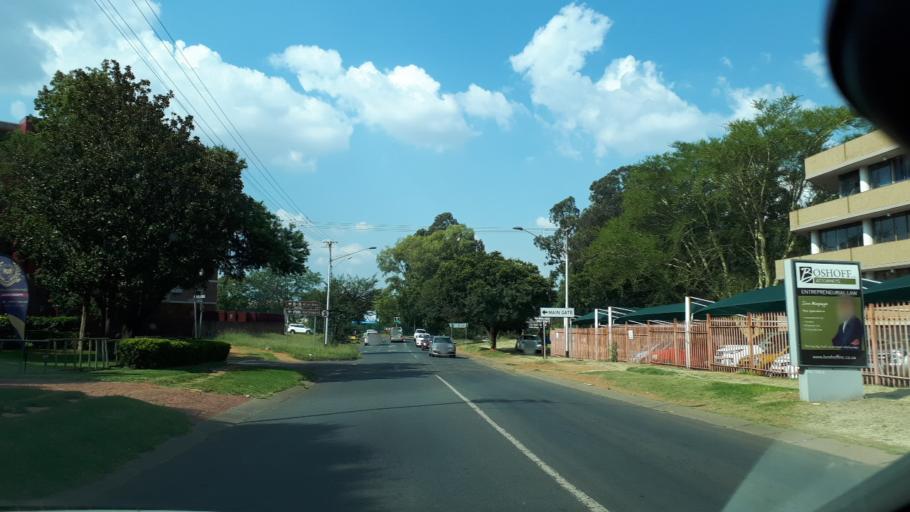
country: ZA
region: Gauteng
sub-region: City of Tshwane Metropolitan Municipality
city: Pretoria
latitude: -25.7775
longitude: 28.2820
